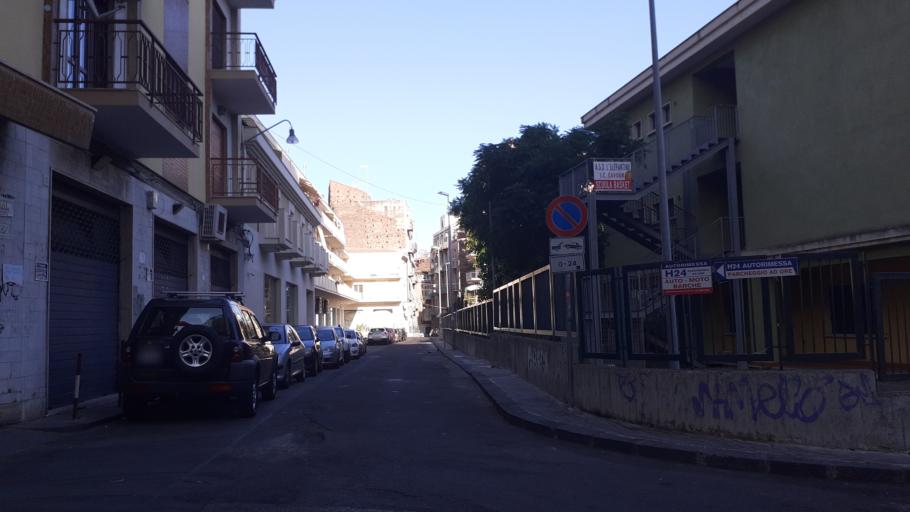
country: IT
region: Sicily
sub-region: Catania
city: Catania
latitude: 37.5131
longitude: 15.0864
